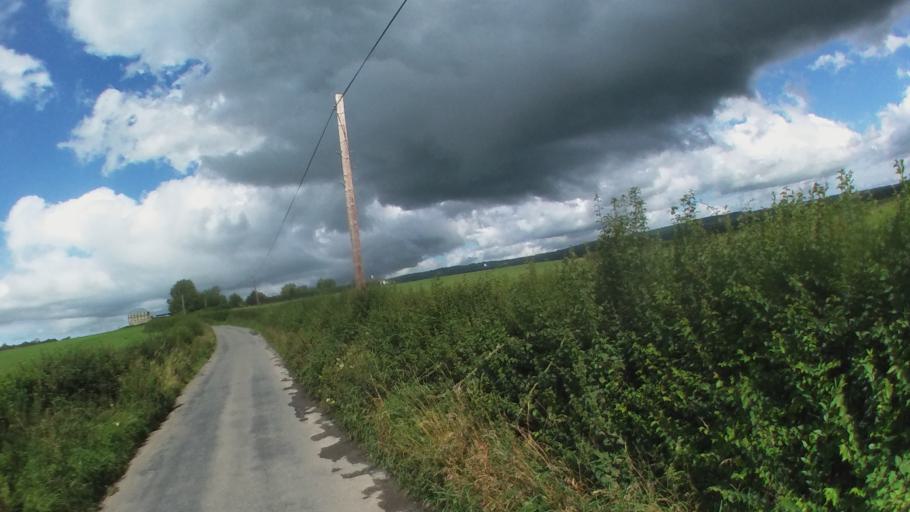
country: IE
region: Leinster
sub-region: Kilkenny
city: Kilkenny
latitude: 52.6880
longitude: -7.2183
